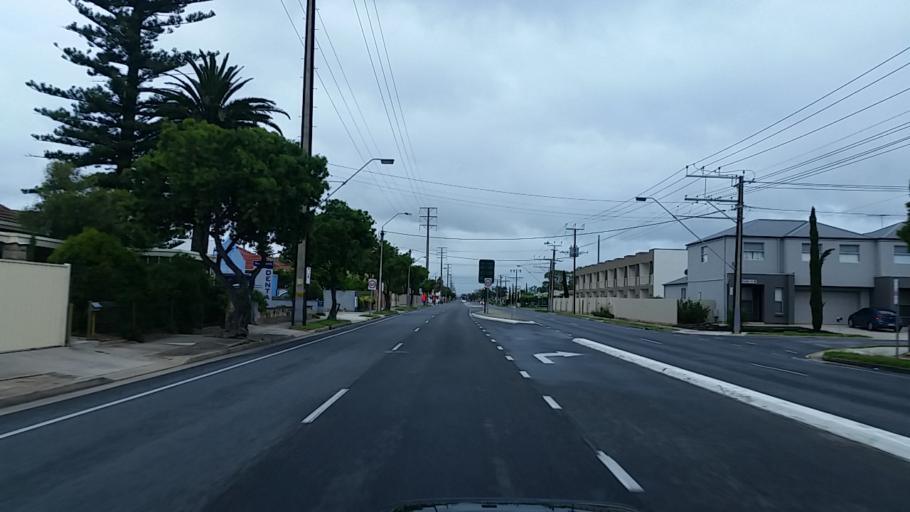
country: AU
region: South Australia
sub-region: Charles Sturt
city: Royal Park
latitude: -34.8807
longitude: 138.5129
